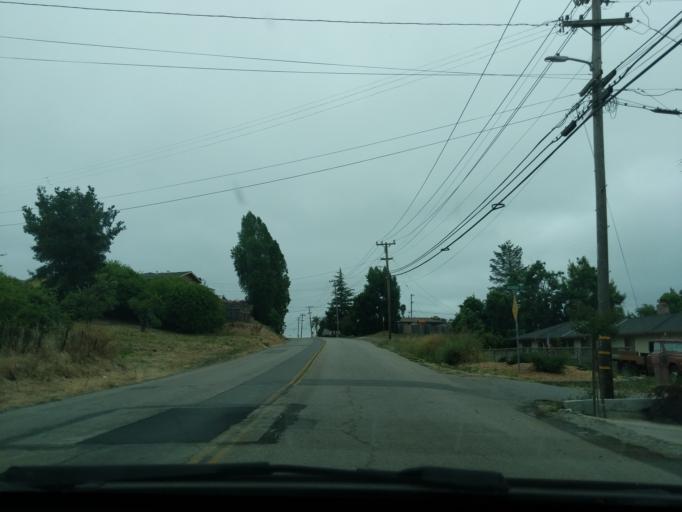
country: US
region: California
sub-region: Santa Cruz County
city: Interlaken
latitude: 36.9334
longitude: -121.7352
